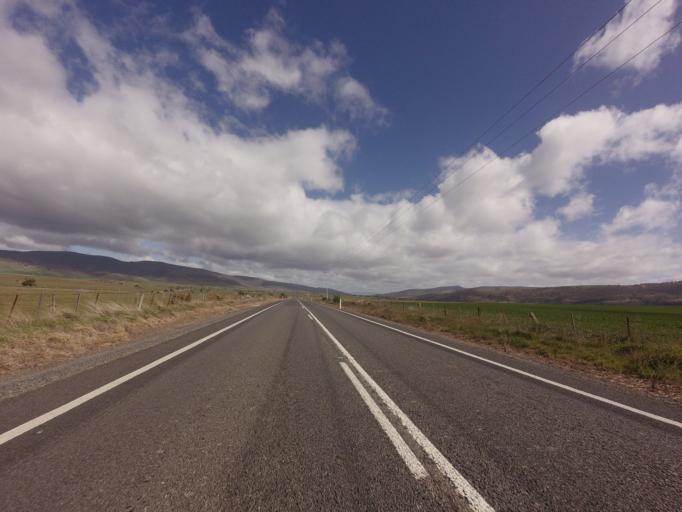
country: AU
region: Tasmania
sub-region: Northern Midlands
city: Evandale
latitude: -41.8014
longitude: 147.6908
